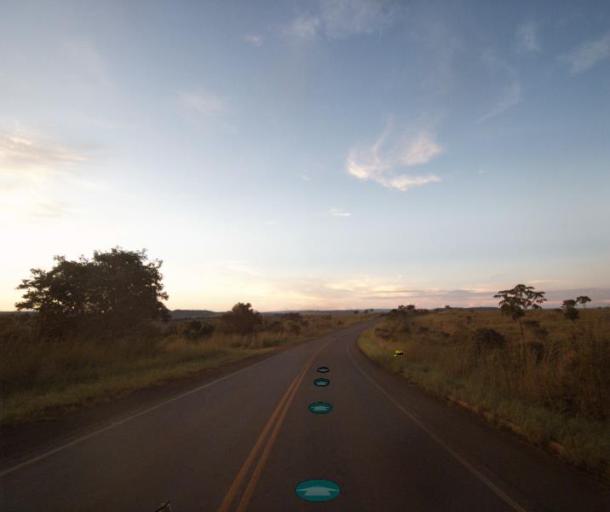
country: BR
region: Goias
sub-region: Pirenopolis
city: Pirenopolis
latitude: -16.0073
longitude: -48.8421
